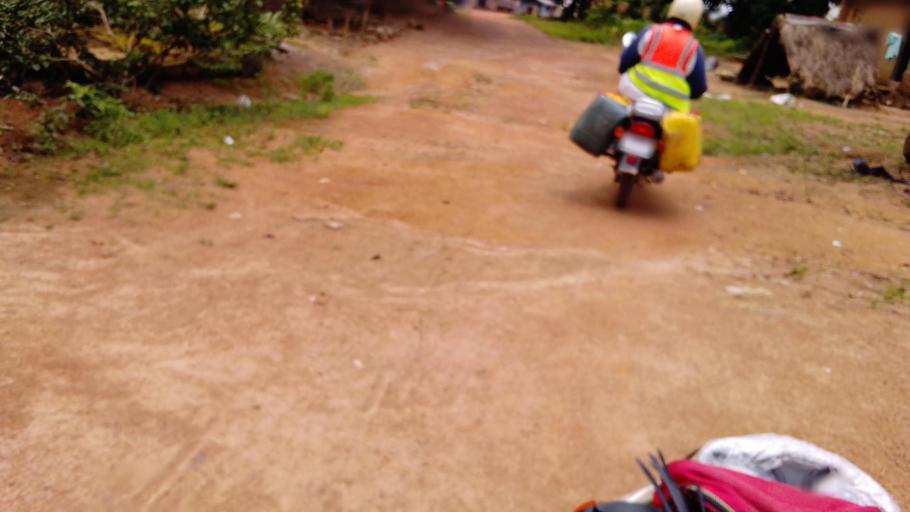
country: SL
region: Eastern Province
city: Koidu
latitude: 8.6596
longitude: -10.9406
